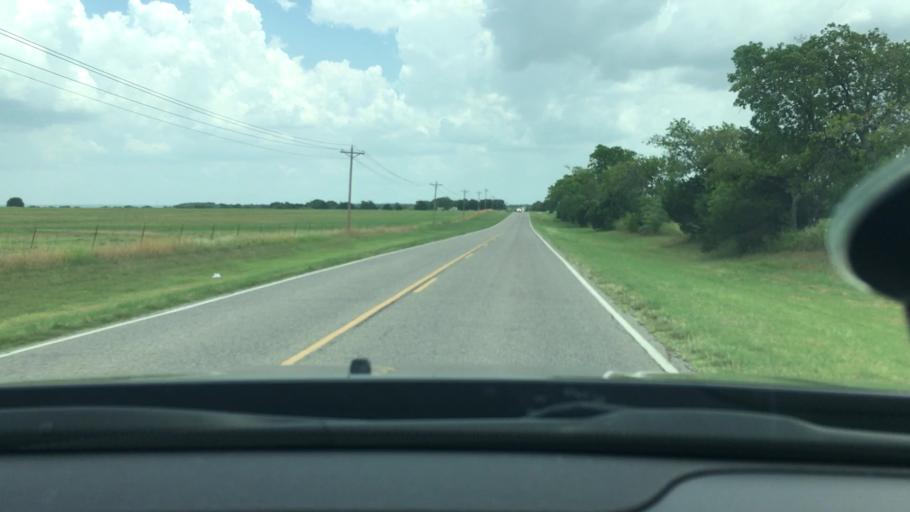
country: US
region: Oklahoma
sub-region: Love County
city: Marietta
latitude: 33.9403
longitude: -97.0560
